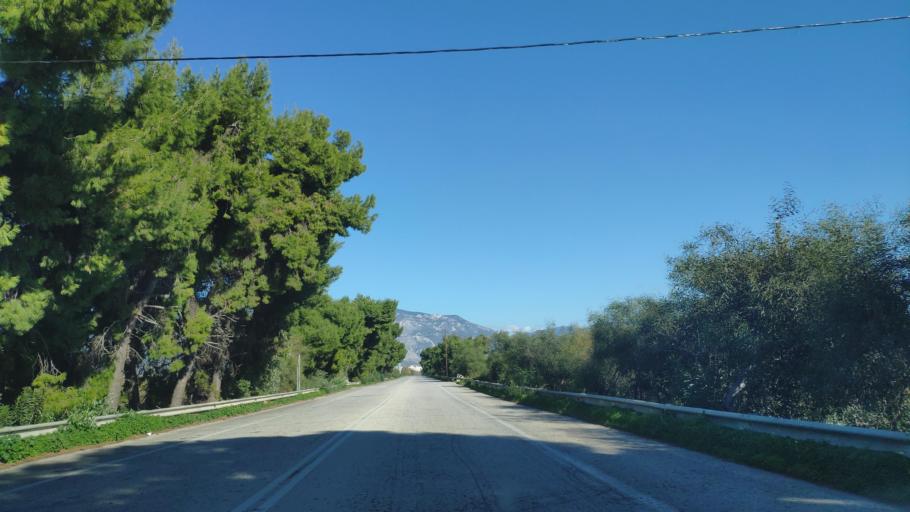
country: GR
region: Peloponnese
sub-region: Nomos Korinthias
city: Examilia
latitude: 37.9229
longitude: 22.9129
